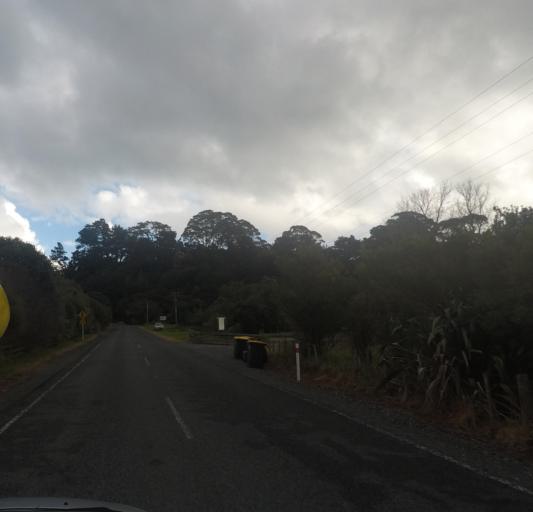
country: NZ
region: Auckland
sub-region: Auckland
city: Warkworth
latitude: -36.3766
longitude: 174.7954
